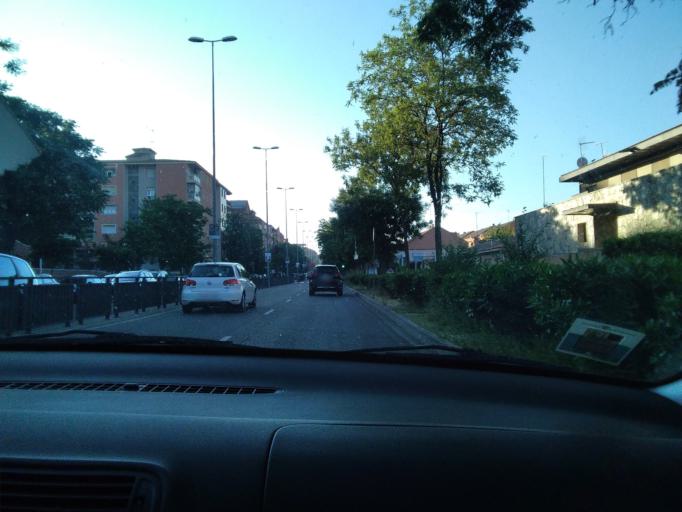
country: ES
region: Castille-La Mancha
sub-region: Province of Toledo
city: Toledo
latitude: 39.8700
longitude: -4.0335
